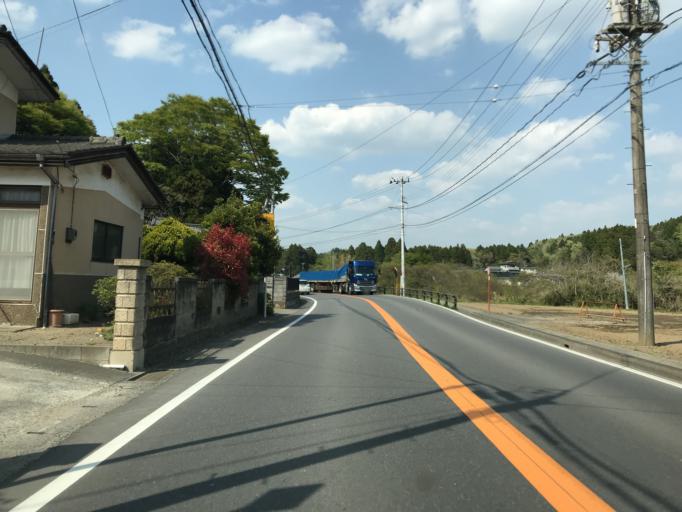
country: JP
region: Ibaraki
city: Kitaibaraki
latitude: 36.9403
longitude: 140.7694
